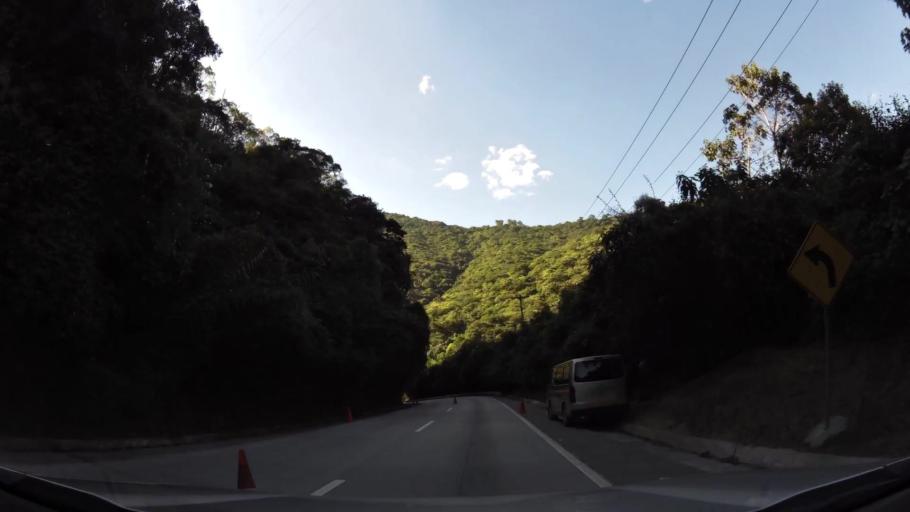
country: GT
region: Sacatepequez
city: Santa Lucia Milpas Altas
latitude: 14.5663
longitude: -90.6987
